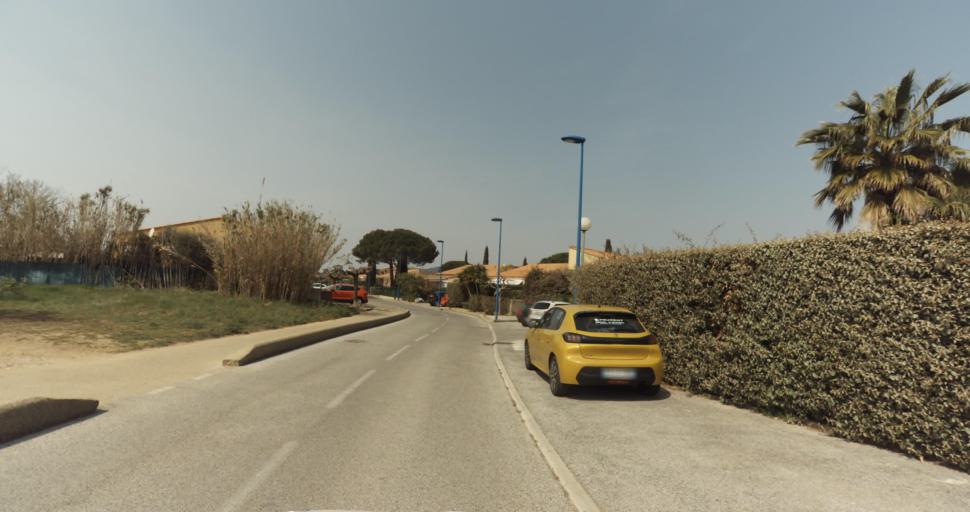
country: FR
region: Provence-Alpes-Cote d'Azur
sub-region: Departement du Var
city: Bormes-les-Mimosas
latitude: 43.1334
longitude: 6.3434
